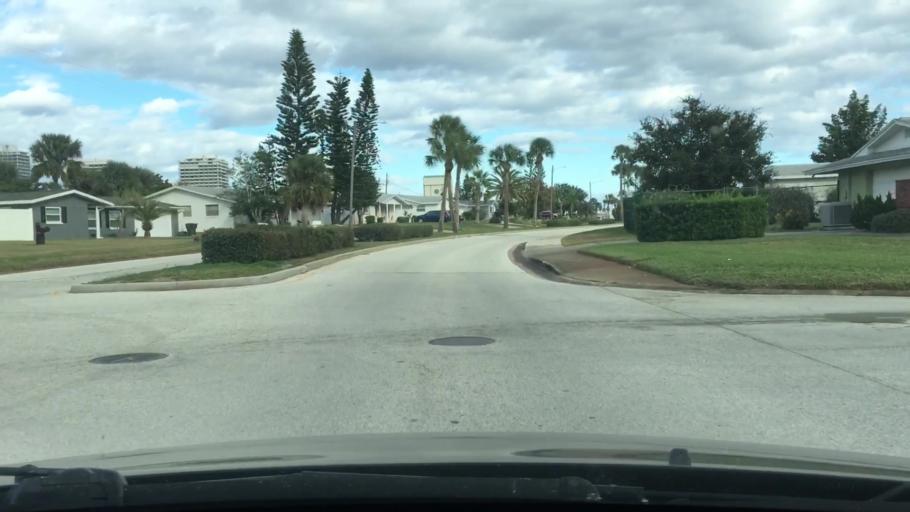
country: US
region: Florida
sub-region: Volusia County
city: Holly Hill
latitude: 29.2626
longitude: -81.0331
